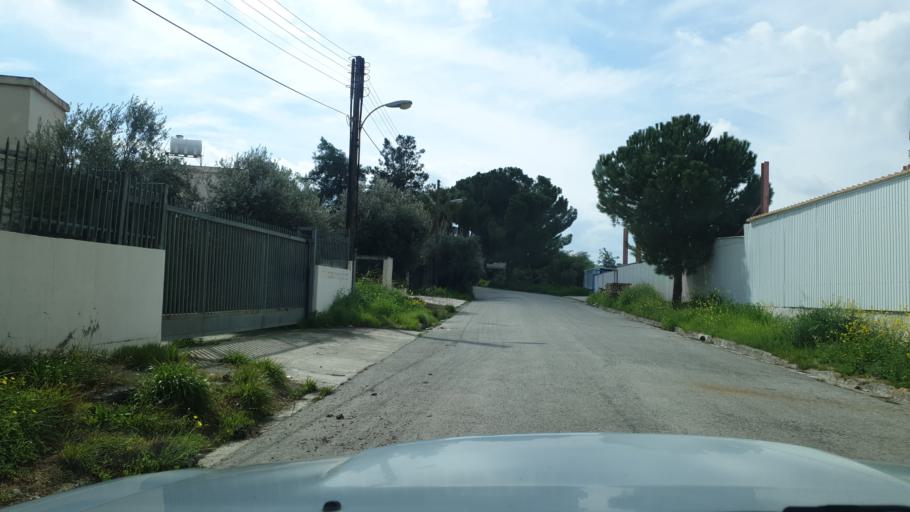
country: CY
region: Lefkosia
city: Nicosia
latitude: 35.1271
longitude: 33.3622
